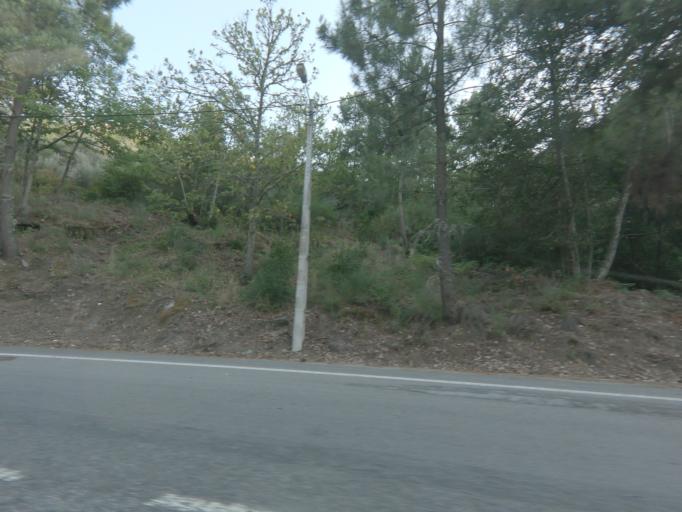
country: PT
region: Viseu
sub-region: Tabuaco
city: Tabuaco
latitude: 41.1165
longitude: -7.5786
